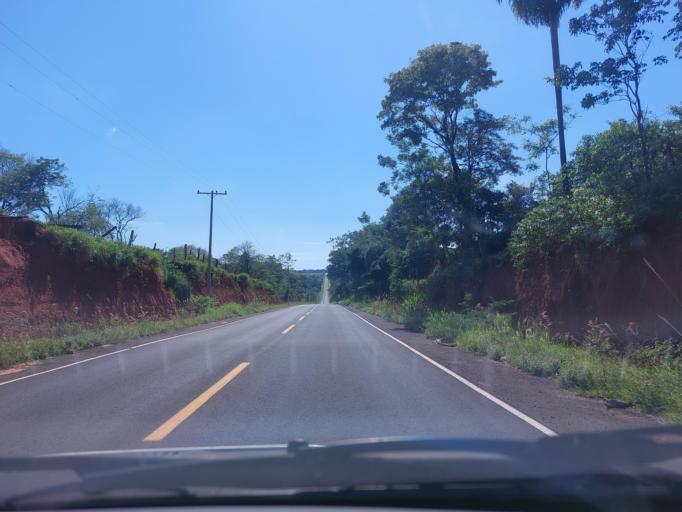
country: PY
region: San Pedro
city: Guayaybi
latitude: -24.5546
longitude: -56.5196
